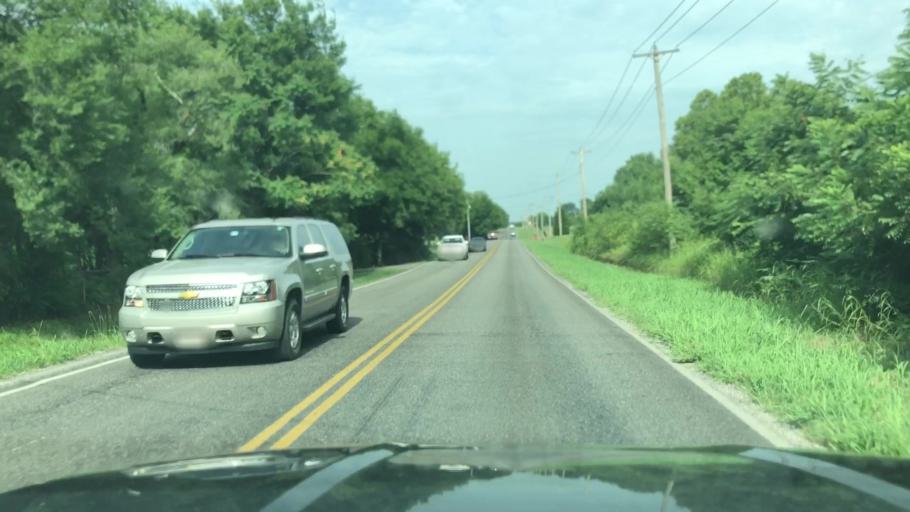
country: US
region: Oklahoma
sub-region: Tulsa County
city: Oakhurst
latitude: 36.0902
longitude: -96.0976
